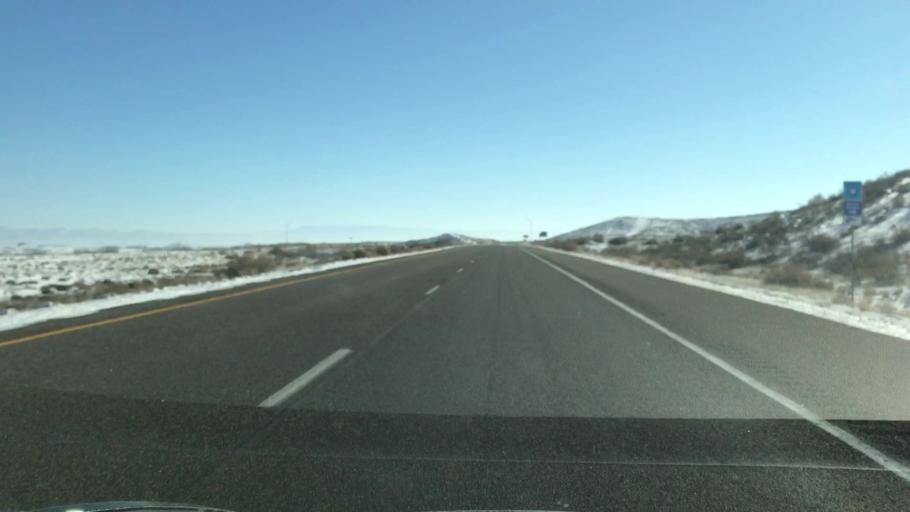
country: US
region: Colorado
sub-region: Mesa County
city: Loma
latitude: 39.2174
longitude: -108.8766
